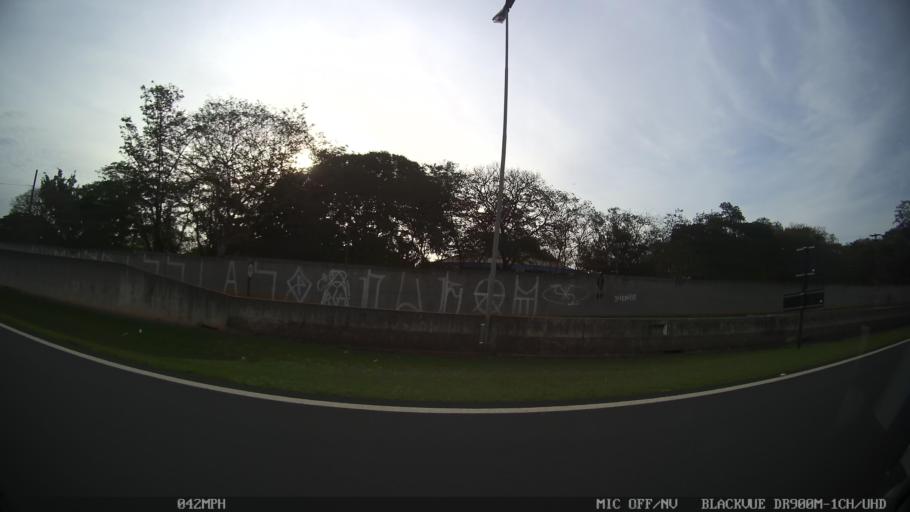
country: BR
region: Sao Paulo
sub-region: Limeira
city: Limeira
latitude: -22.5695
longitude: -47.4419
